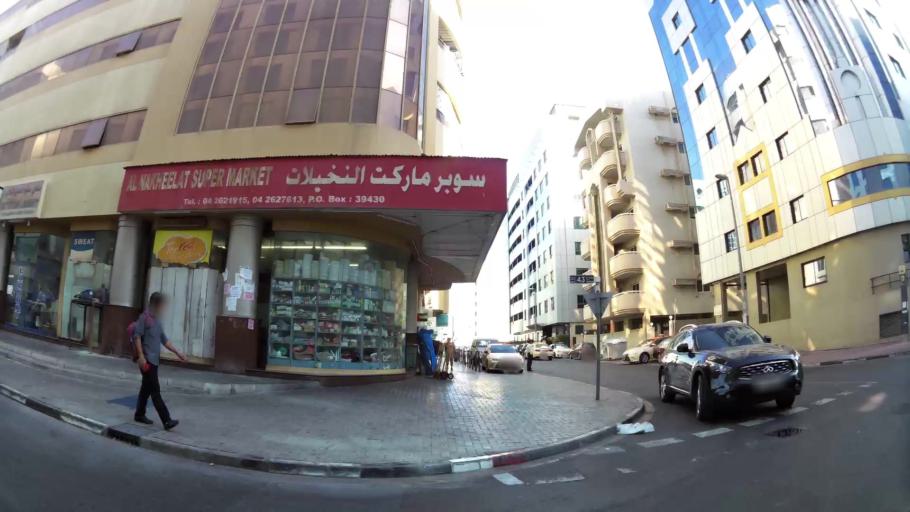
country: AE
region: Ash Shariqah
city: Sharjah
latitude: 25.2632
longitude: 55.3273
